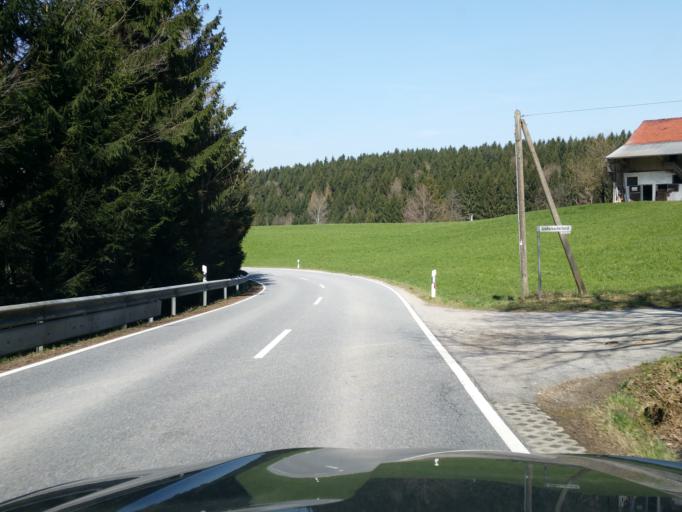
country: DE
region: Bavaria
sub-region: Upper Bavaria
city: Kirchberg
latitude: 48.4451
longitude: 12.0542
